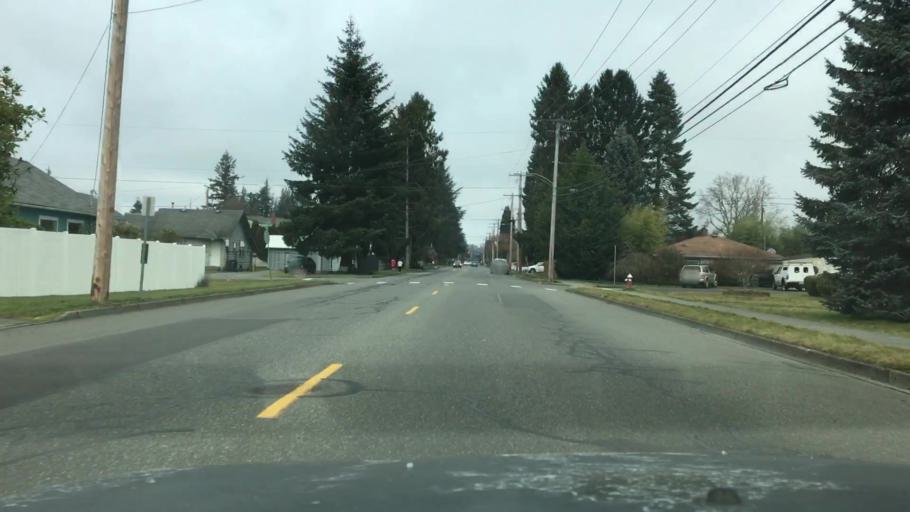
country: US
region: Washington
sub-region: Skagit County
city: Sedro-Woolley
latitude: 48.5002
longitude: -122.2259
